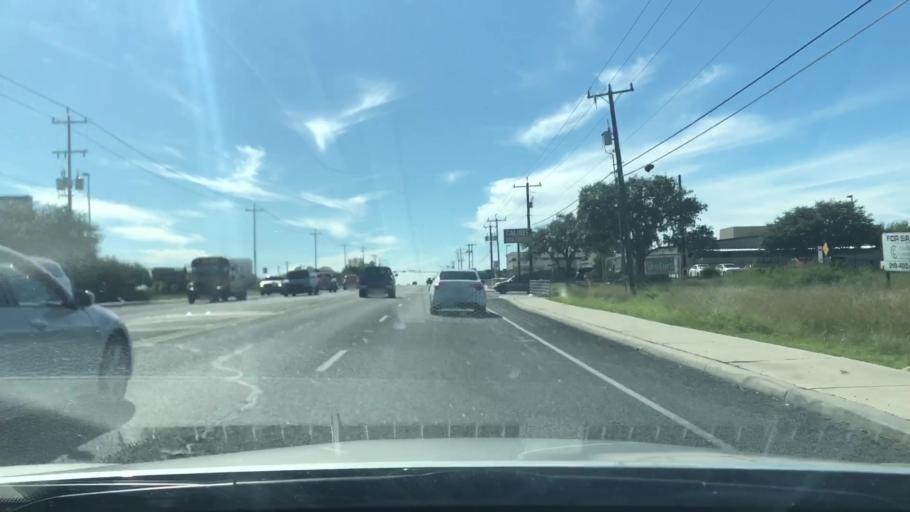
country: US
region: Texas
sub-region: Bexar County
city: Converse
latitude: 29.4913
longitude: -98.3351
